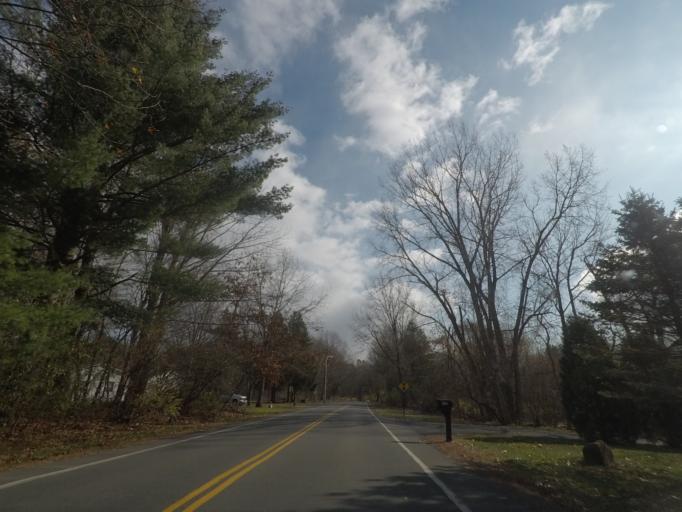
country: US
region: New York
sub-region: Saratoga County
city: Country Knolls
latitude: 42.8935
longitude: -73.8112
